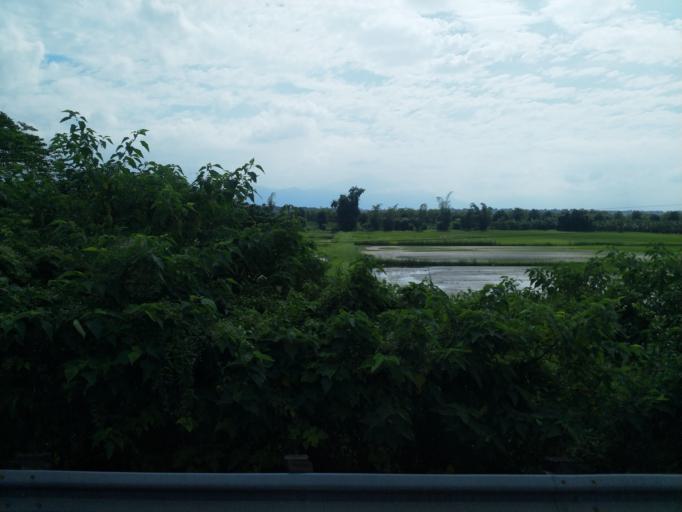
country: TW
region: Taiwan
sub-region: Pingtung
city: Pingtung
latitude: 22.8653
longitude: 120.4921
